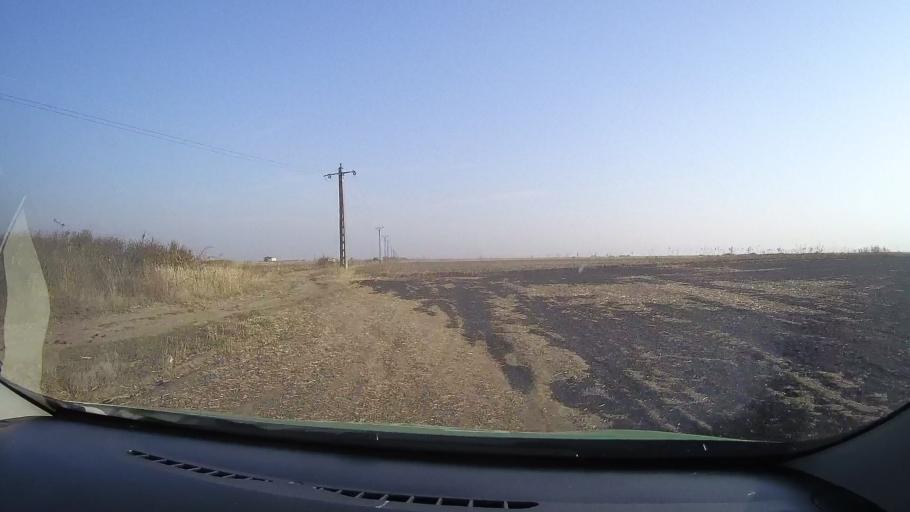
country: RO
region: Arad
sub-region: Comuna Pilu
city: Pilu
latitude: 46.5403
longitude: 21.3274
